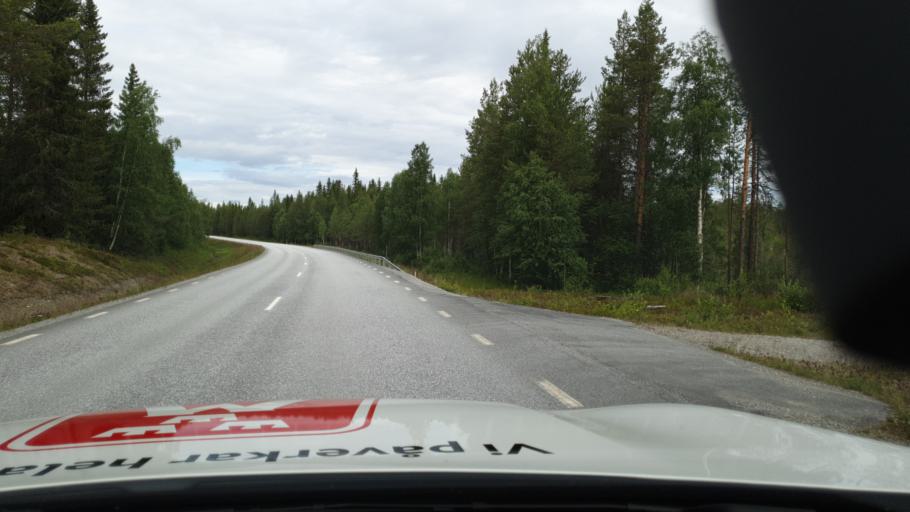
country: SE
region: Vaesterbotten
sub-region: Storumans Kommun
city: Storuman
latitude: 65.2134
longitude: 16.9877
